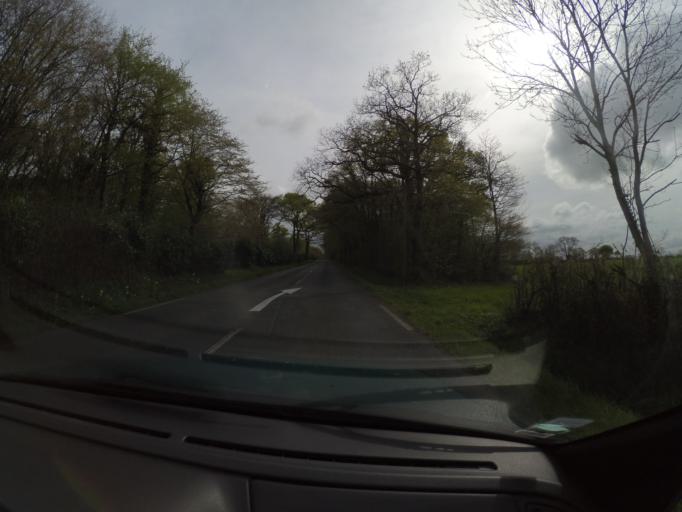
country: FR
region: Pays de la Loire
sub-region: Departement de Maine-et-Loire
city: Saint-Laurent-des-Autels
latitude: 47.2735
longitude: -1.1972
